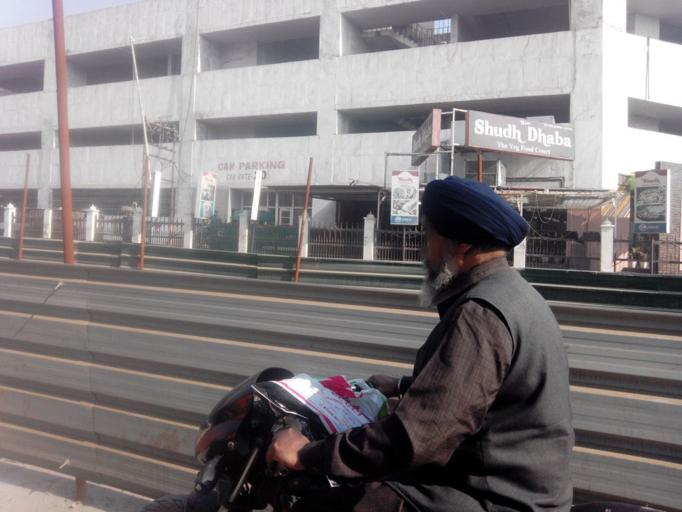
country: IN
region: Punjab
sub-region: Amritsar
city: Amritsar
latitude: 31.6239
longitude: 74.8795
